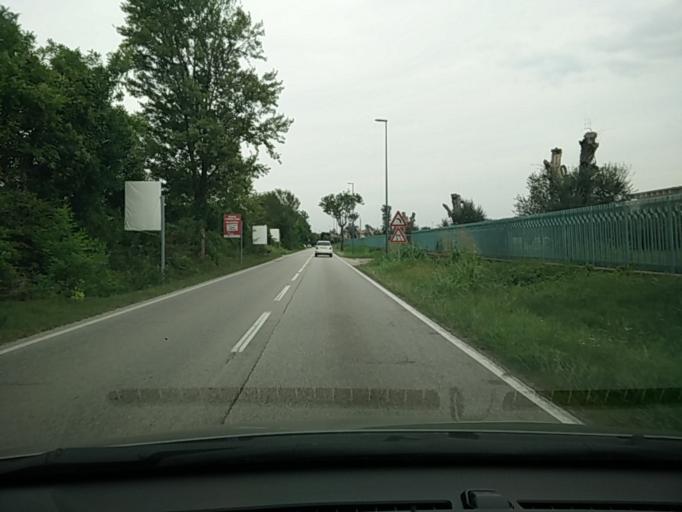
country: IT
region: Veneto
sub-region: Provincia di Treviso
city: Castagnole
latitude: 45.6678
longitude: 12.1969
